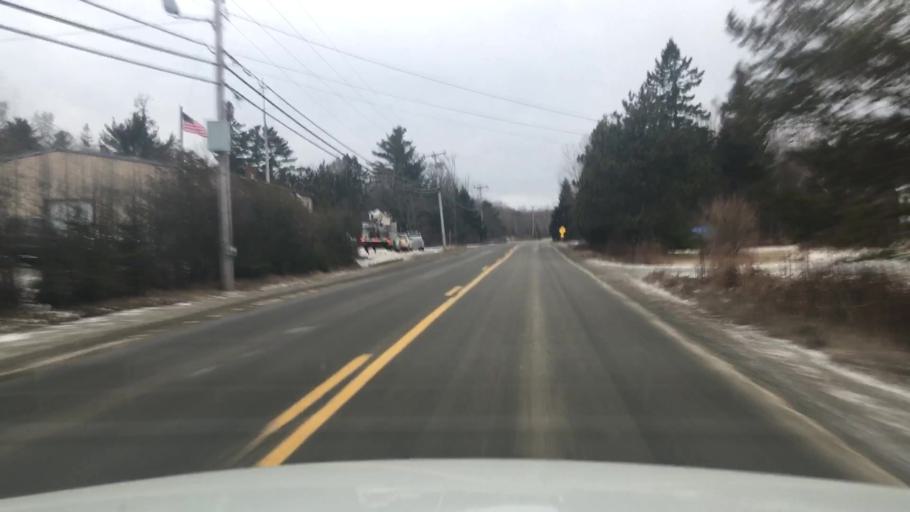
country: US
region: Maine
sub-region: Hancock County
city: Trenton
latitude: 44.5002
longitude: -68.3566
